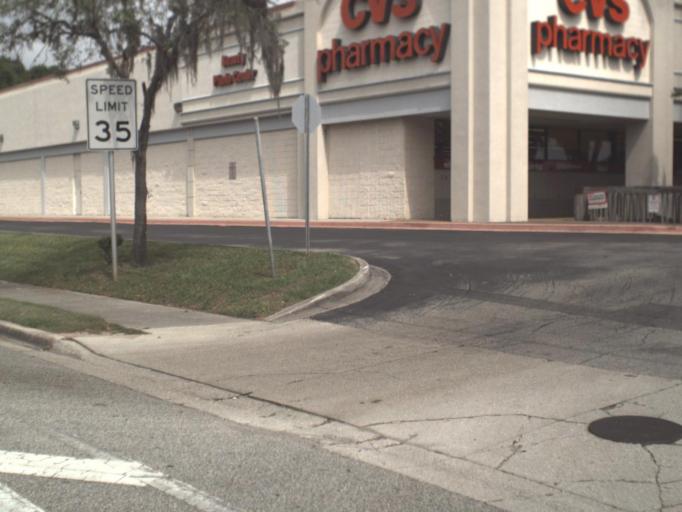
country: US
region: Florida
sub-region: Clay County
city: Orange Park
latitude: 30.1660
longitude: -81.7020
